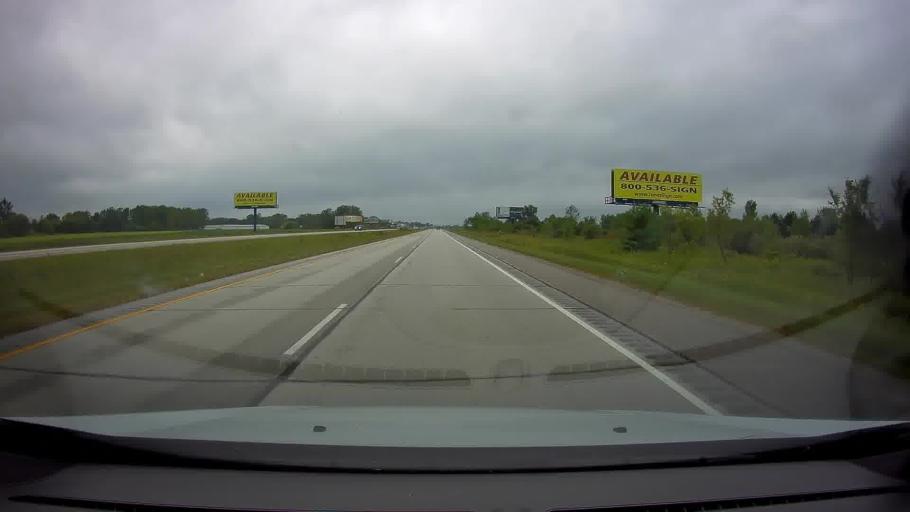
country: US
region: Wisconsin
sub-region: Brown County
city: Pulaski
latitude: 44.5986
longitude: -88.2310
